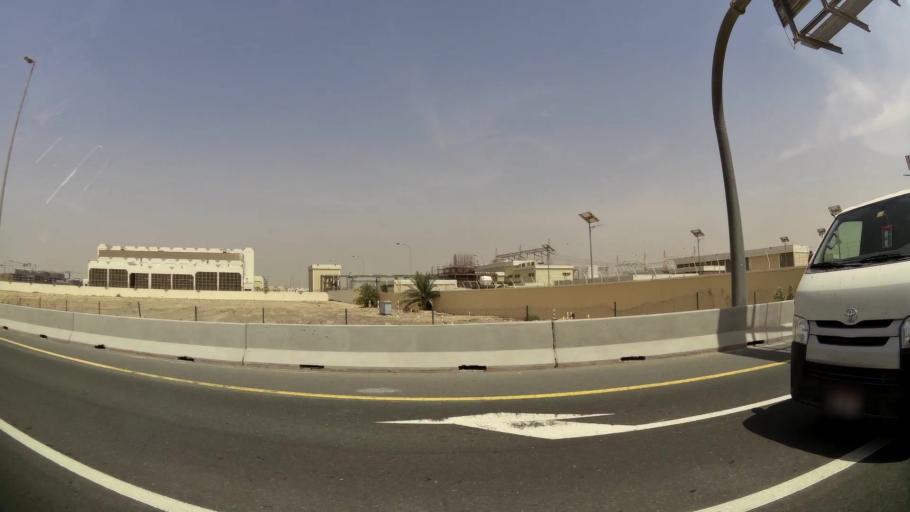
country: AE
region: Ash Shariqah
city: Sharjah
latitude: 25.2330
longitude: 55.4061
